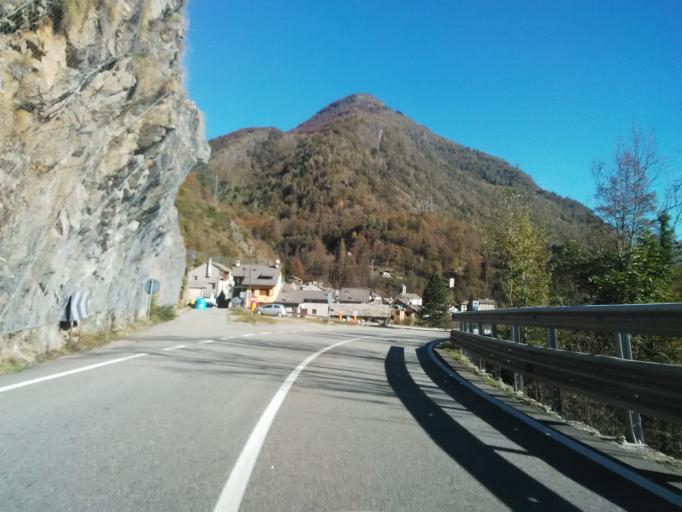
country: IT
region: Piedmont
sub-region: Provincia di Vercelli
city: Balmuccia
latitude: 45.8166
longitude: 8.1349
